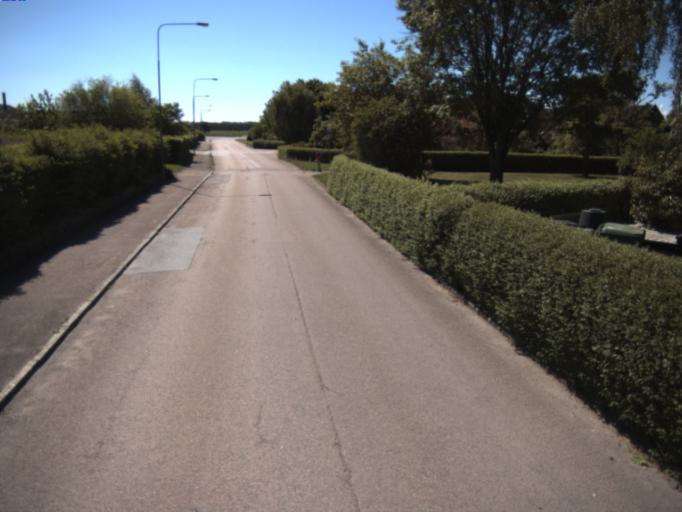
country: SE
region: Skane
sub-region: Helsingborg
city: Barslov
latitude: 56.0068
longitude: 12.8017
